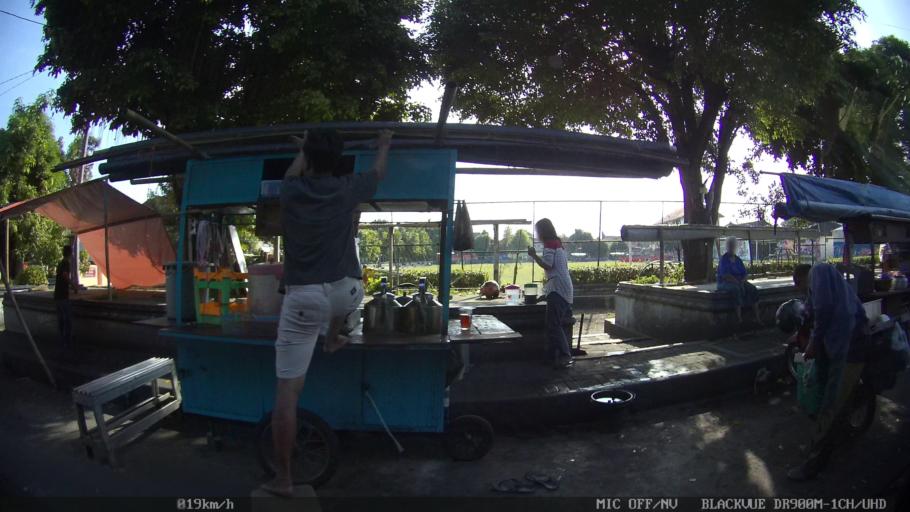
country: ID
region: Daerah Istimewa Yogyakarta
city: Yogyakarta
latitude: -7.8206
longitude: 110.3806
